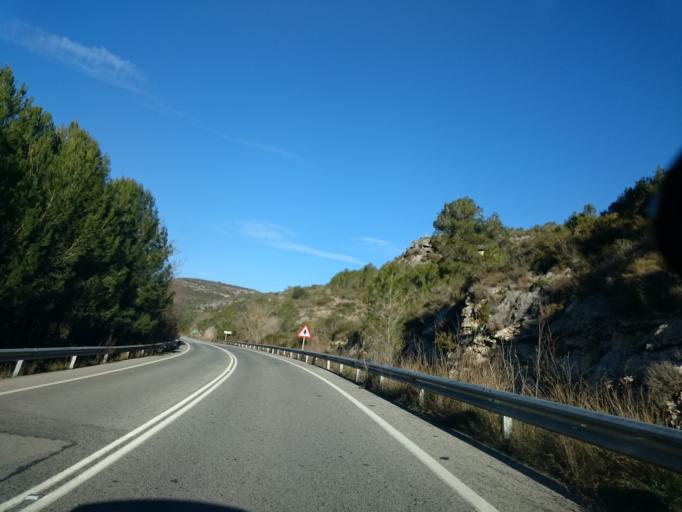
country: ES
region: Catalonia
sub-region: Provincia de Barcelona
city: Sant Pere de Ribes
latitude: 41.3006
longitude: 1.7286
